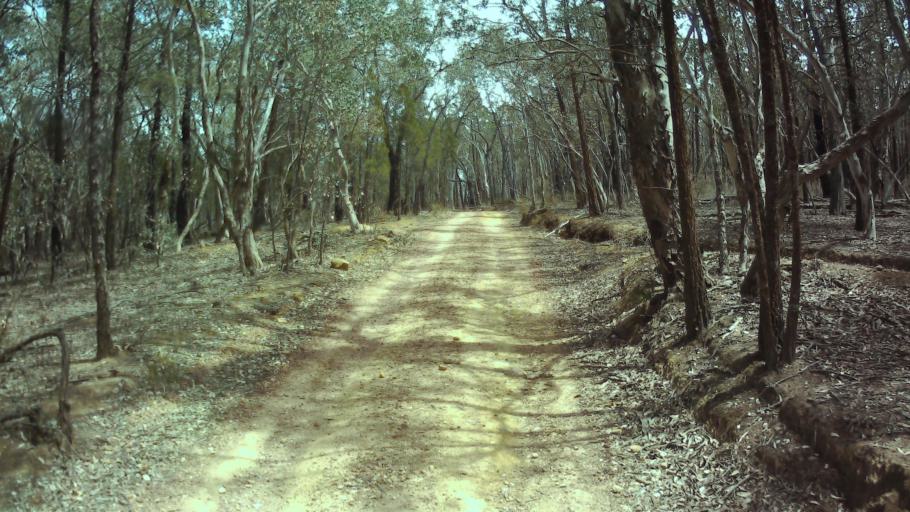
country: AU
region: New South Wales
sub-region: Weddin
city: Grenfell
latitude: -33.8911
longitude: 148.3878
